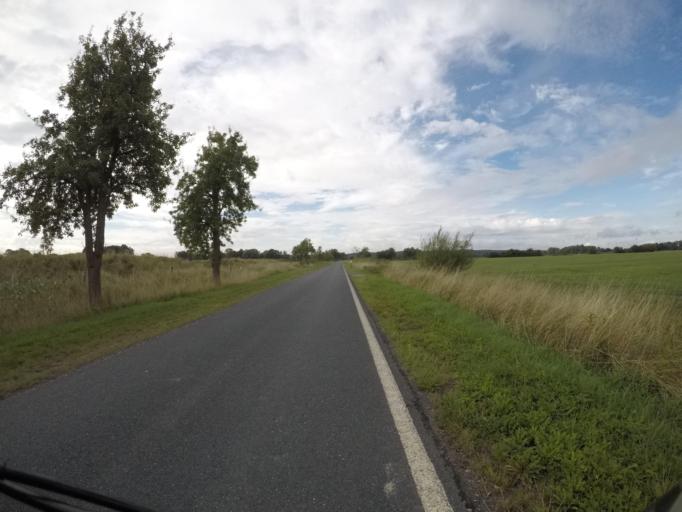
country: DE
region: Lower Saxony
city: Neu Darchau
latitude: 53.2687
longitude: 10.8525
